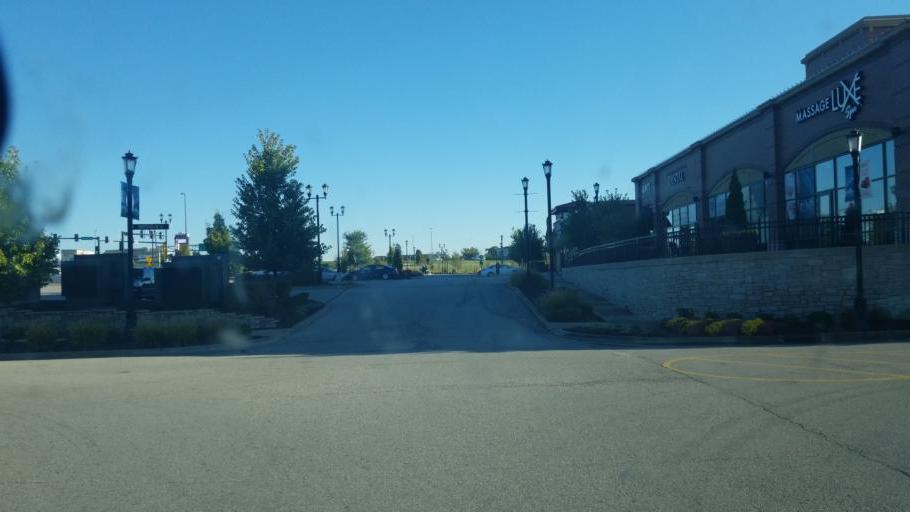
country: US
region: Missouri
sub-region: Saint Charles County
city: Saint Charles
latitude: 38.7657
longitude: -90.4954
